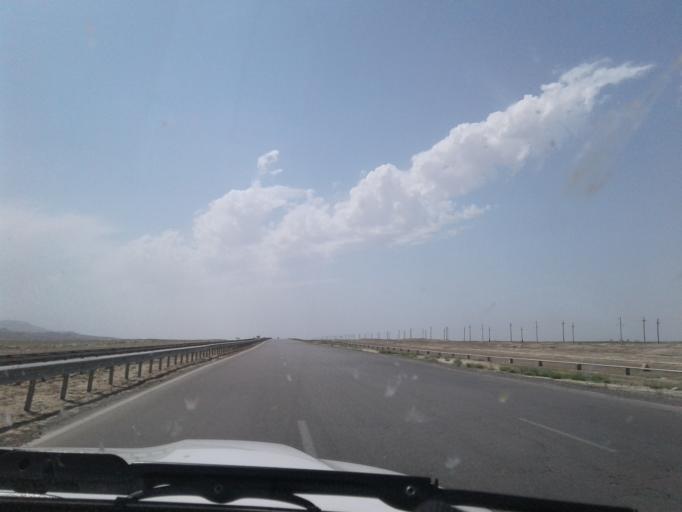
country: IR
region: Razavi Khorasan
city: Dargaz
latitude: 37.7496
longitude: 58.9541
